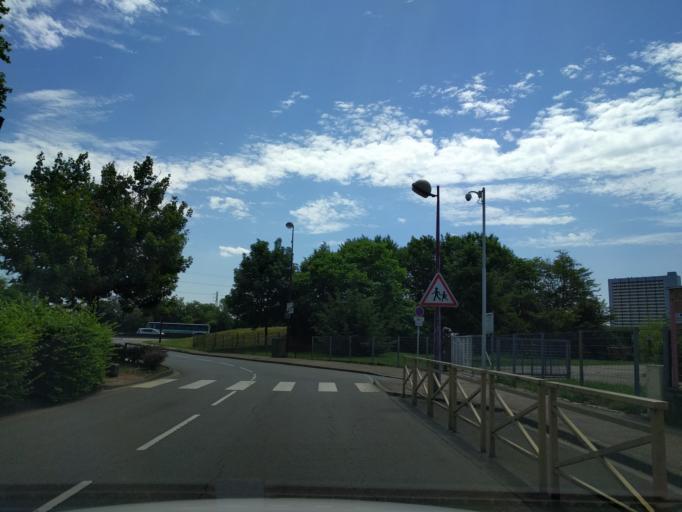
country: FR
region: Lorraine
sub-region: Departement de la Moselle
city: Metz
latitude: 49.1335
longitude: 6.1729
